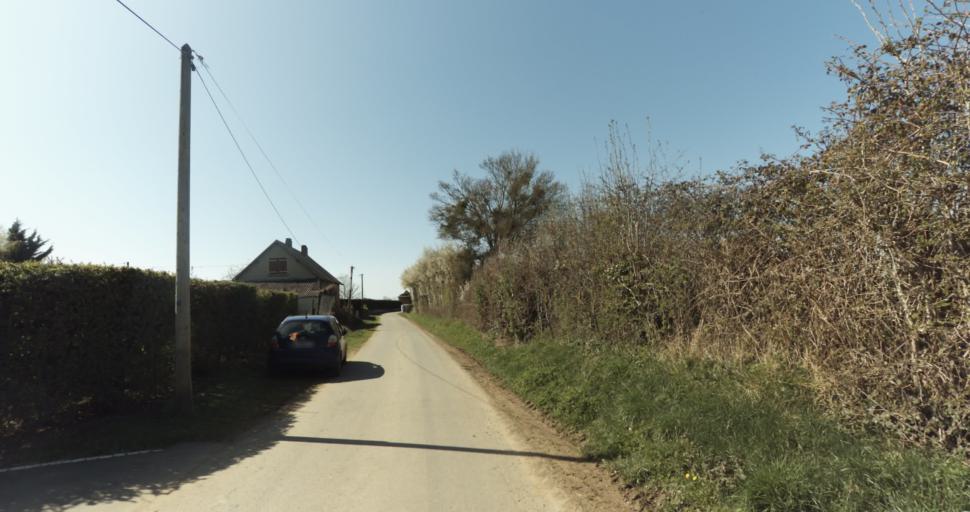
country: FR
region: Lower Normandy
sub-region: Departement du Calvados
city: Saint-Pierre-sur-Dives
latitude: 48.9908
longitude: -0.0233
